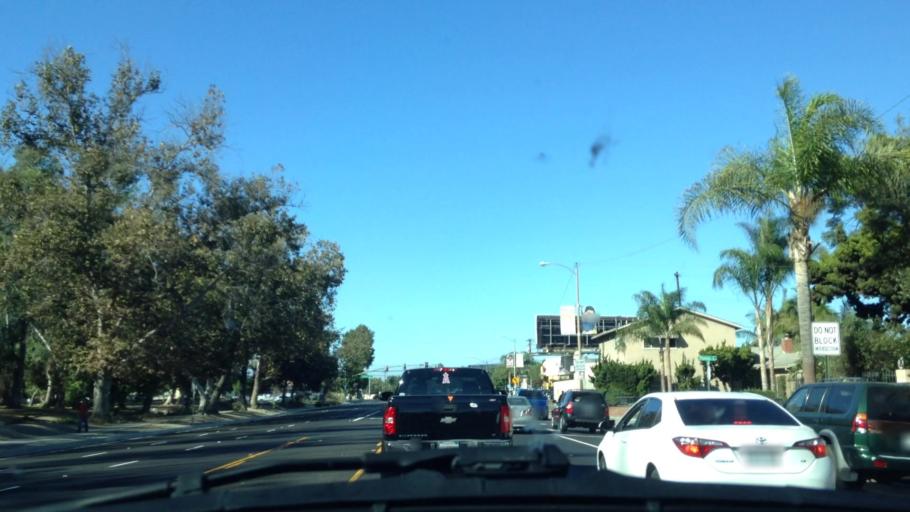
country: US
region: California
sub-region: Orange County
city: Santa Ana
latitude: 33.7254
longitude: -117.9068
